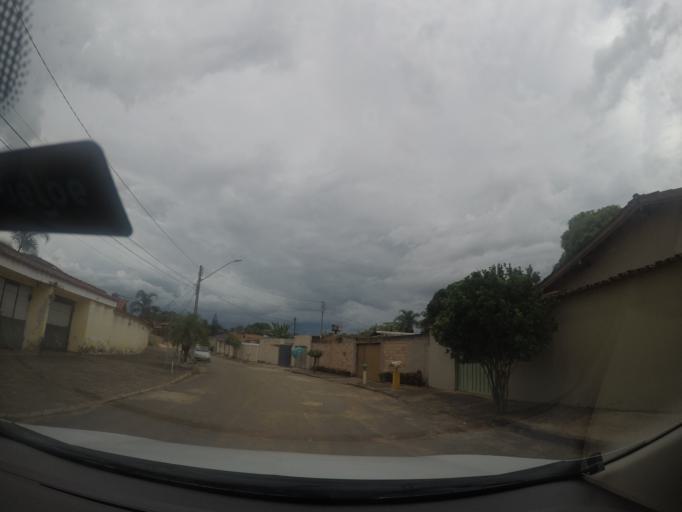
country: BR
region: Goias
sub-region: Goiania
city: Goiania
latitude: -16.6544
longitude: -49.2329
